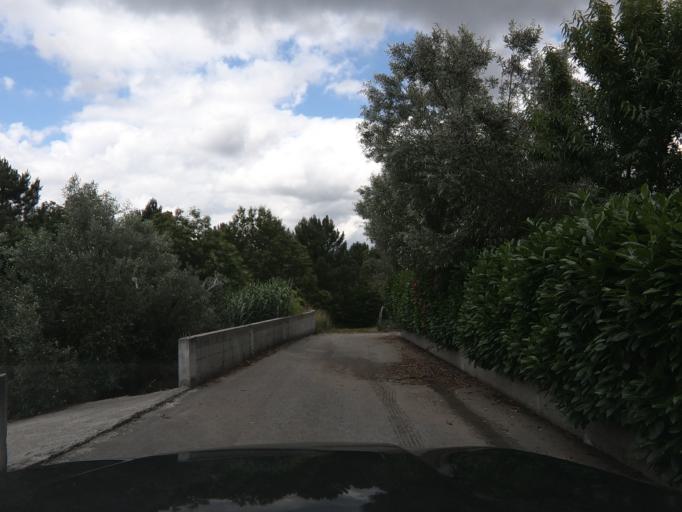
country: PT
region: Vila Real
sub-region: Sabrosa
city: Vilela
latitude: 41.2596
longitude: -7.6539
